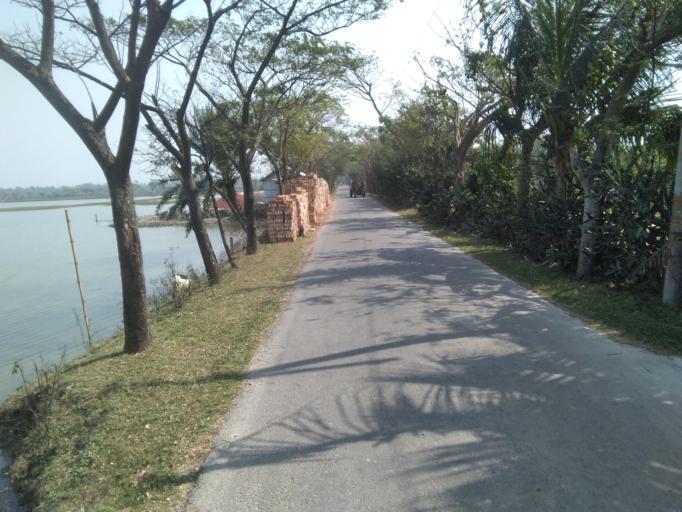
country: IN
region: West Bengal
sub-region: North 24 Parganas
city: Taki
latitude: 22.5933
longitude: 88.9866
